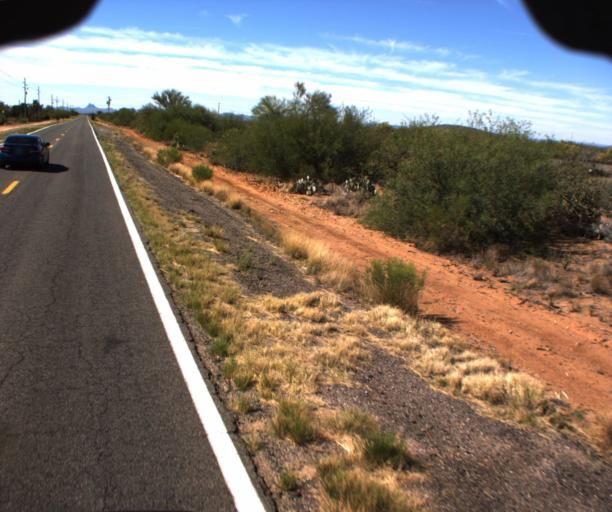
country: US
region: Arizona
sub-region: Yavapai County
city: Congress
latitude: 34.1470
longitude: -112.8426
